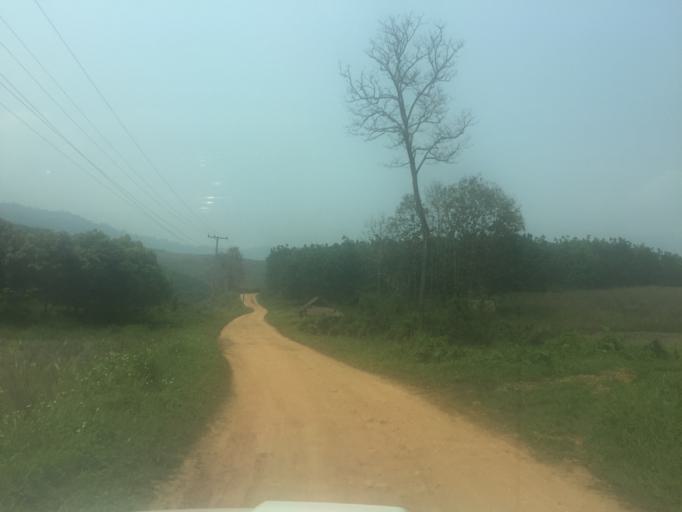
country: TH
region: Phayao
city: Phu Sang
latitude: 19.7724
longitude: 100.5369
